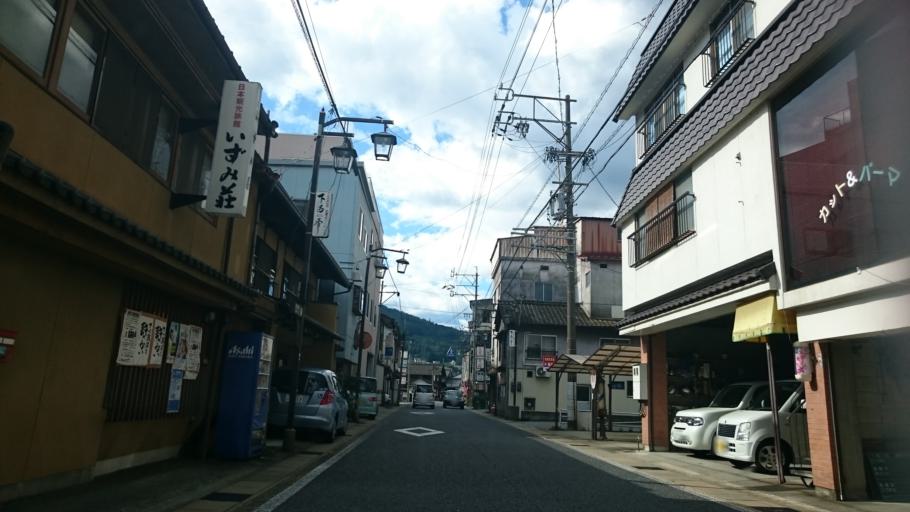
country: JP
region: Gifu
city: Gujo
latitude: 35.8113
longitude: 137.2387
